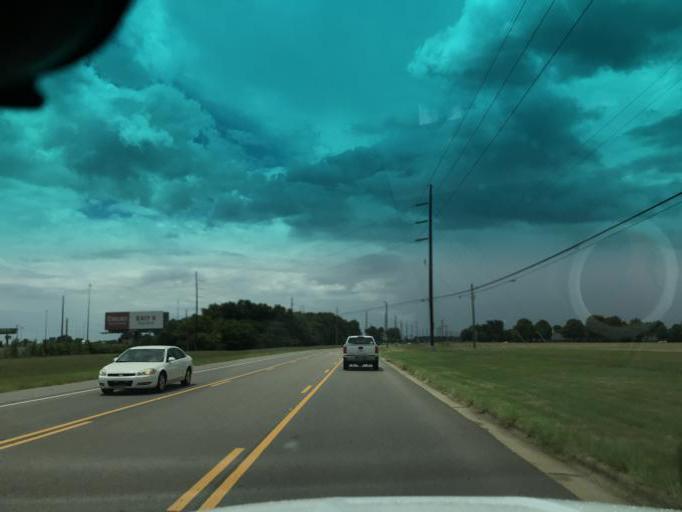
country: US
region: Alabama
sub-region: Montgomery County
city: Pike Road
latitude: 32.3687
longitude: -86.1341
